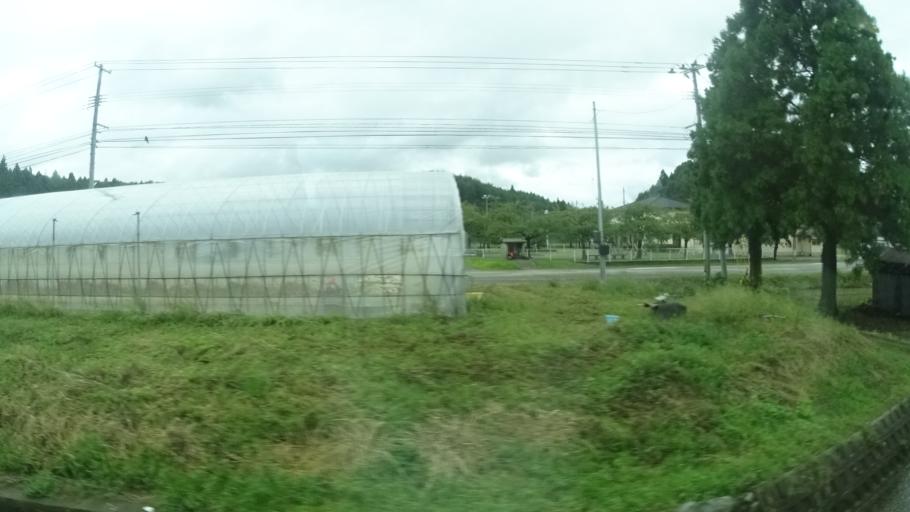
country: JP
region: Niigata
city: Murakami
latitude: 38.2078
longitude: 139.4603
